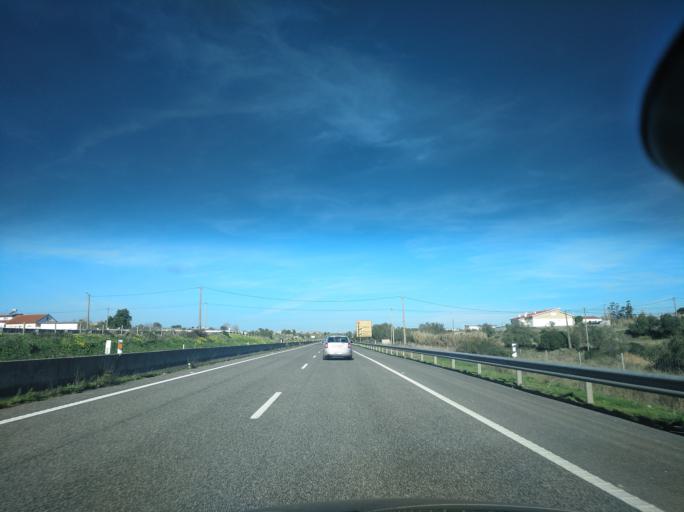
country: PT
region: Lisbon
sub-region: Sintra
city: Pero Pinheiro
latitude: 38.8645
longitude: -9.3370
